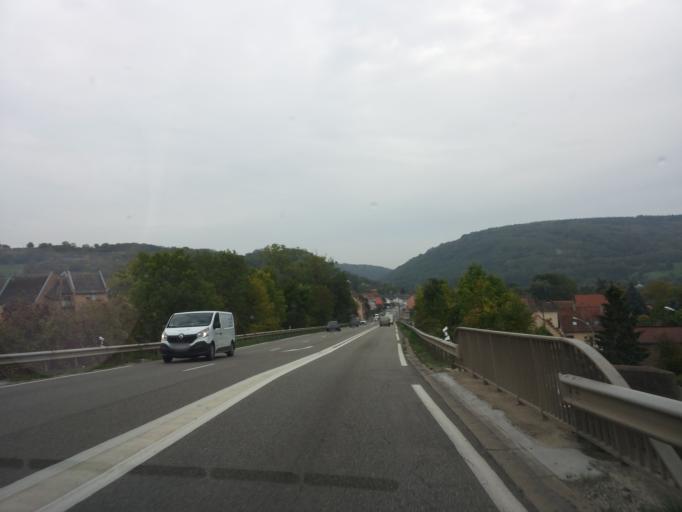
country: FR
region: Alsace
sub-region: Departement du Bas-Rhin
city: Wasselonne
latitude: 48.6412
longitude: 7.4520
